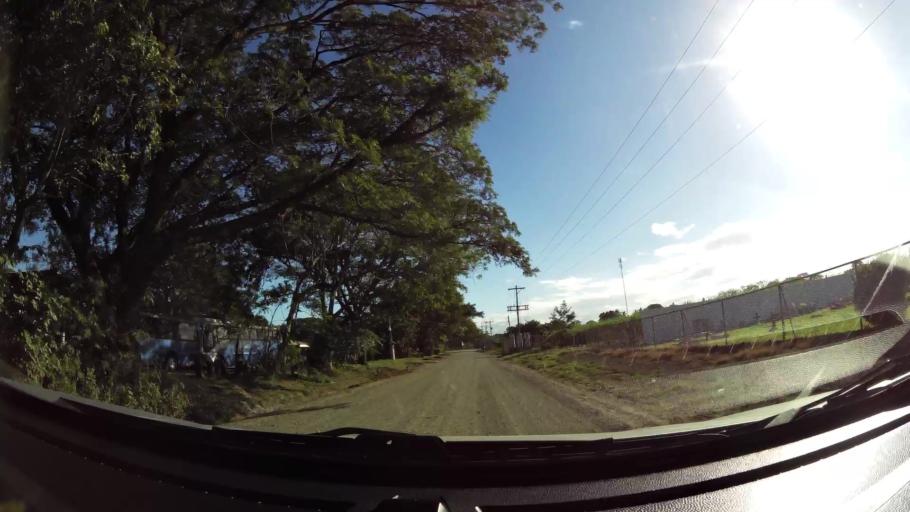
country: CR
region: Guanacaste
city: Belen
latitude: 10.4868
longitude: -85.5697
